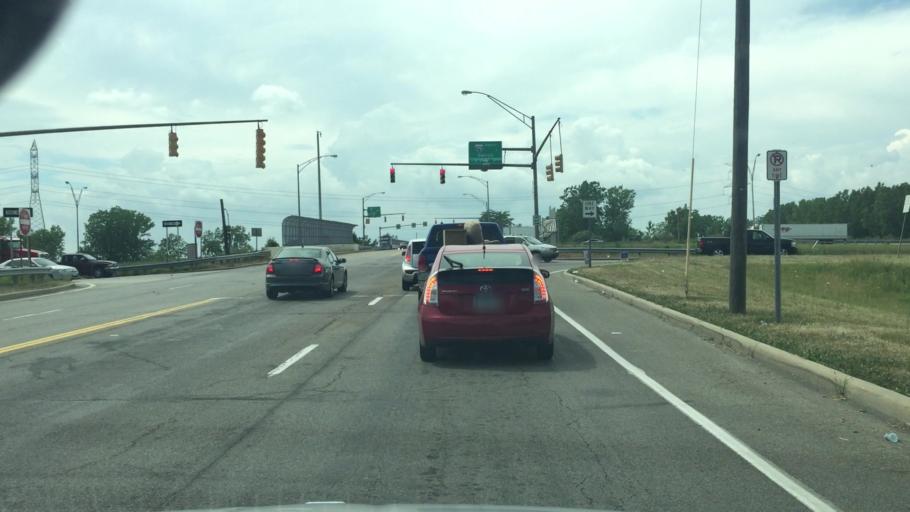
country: US
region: Ohio
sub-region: Lucas County
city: Oregon
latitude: 41.7210
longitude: -83.4999
